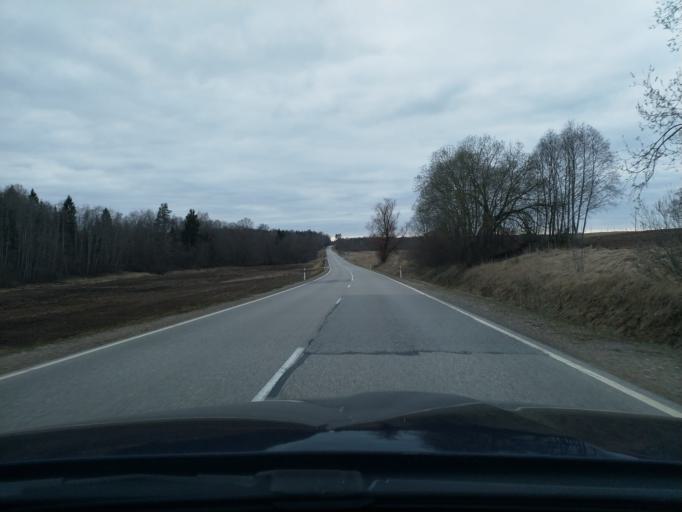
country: LV
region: Kuldigas Rajons
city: Kuldiga
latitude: 56.9654
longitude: 22.0626
